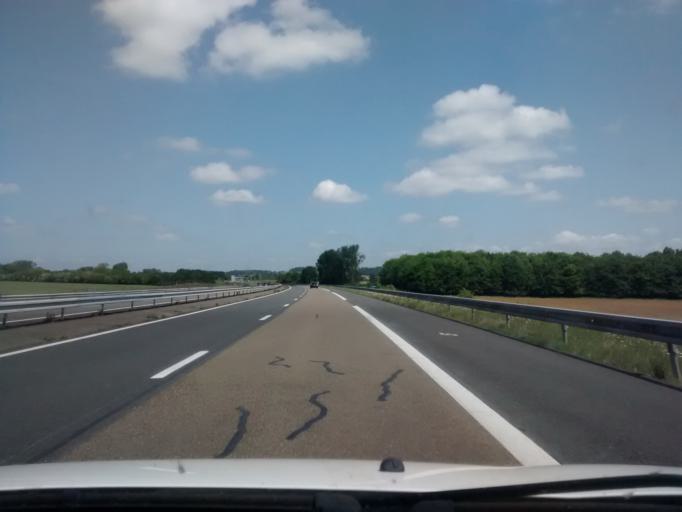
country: FR
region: Pays de la Loire
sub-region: Departement de la Sarthe
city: Louplande
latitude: 48.0146
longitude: -0.0645
